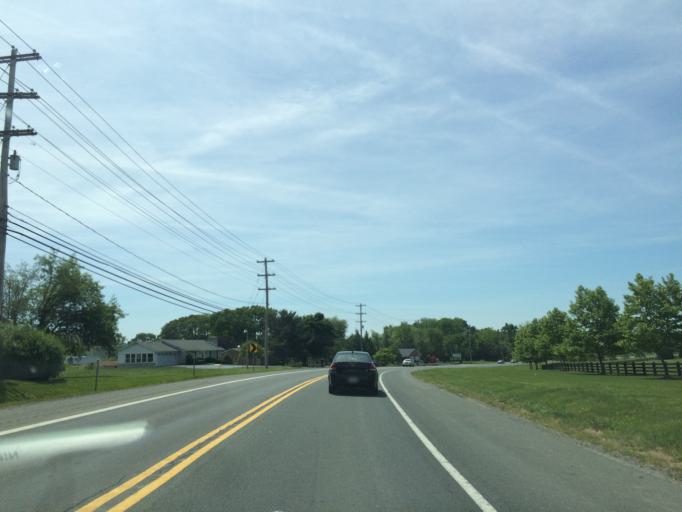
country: US
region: Maryland
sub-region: Washington County
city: Saint James
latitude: 39.5777
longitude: -77.7266
